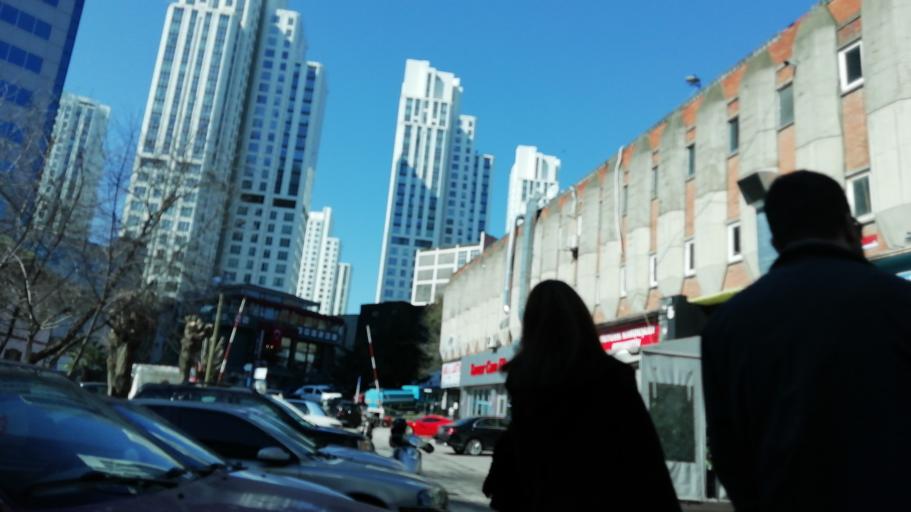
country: TR
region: Istanbul
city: Sisli
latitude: 41.1129
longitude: 29.0189
